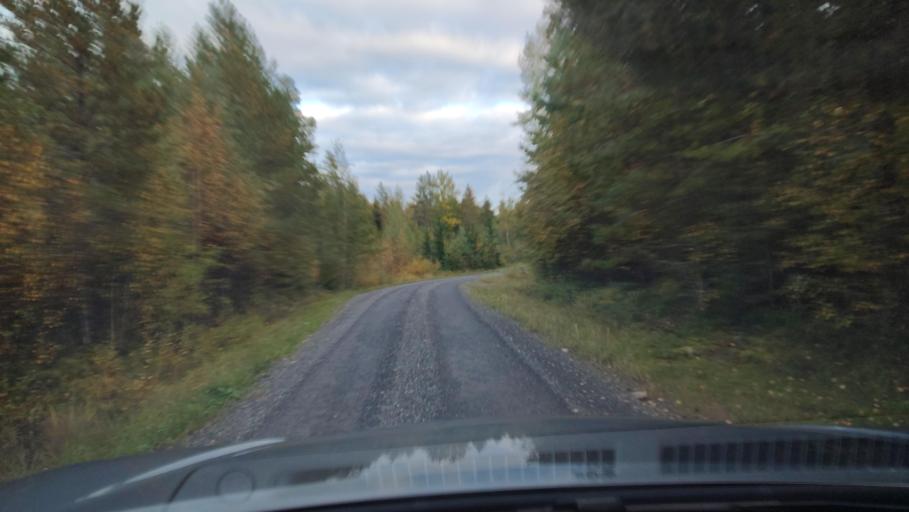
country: FI
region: Ostrobothnia
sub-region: Sydosterbotten
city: Kristinestad
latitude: 62.2315
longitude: 21.4168
